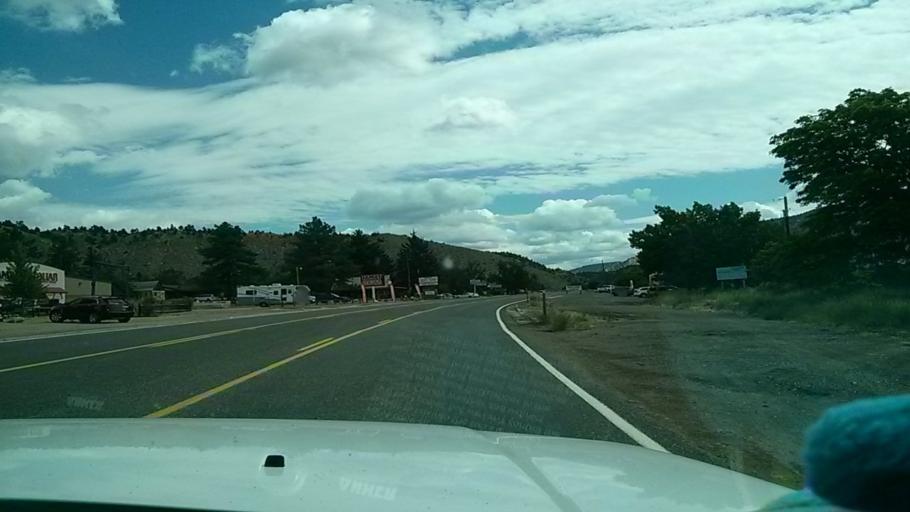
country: US
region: Utah
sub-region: Kane County
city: Kanab
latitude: 37.2709
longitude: -112.6498
